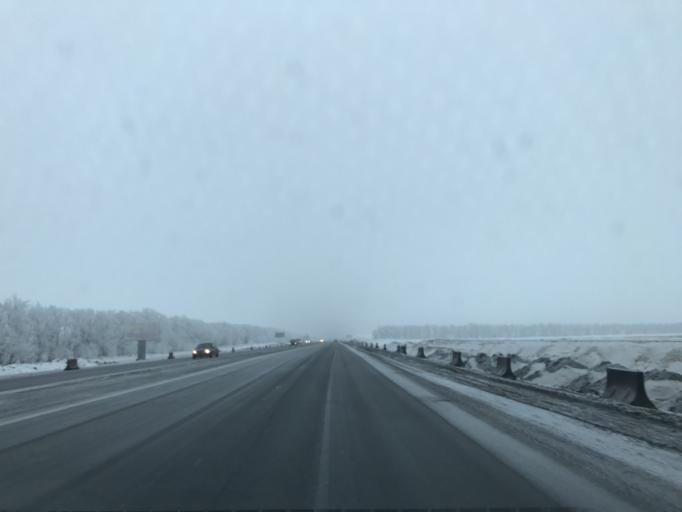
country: RU
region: Rostov
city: Grushevskaya
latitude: 47.5043
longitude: 39.9707
